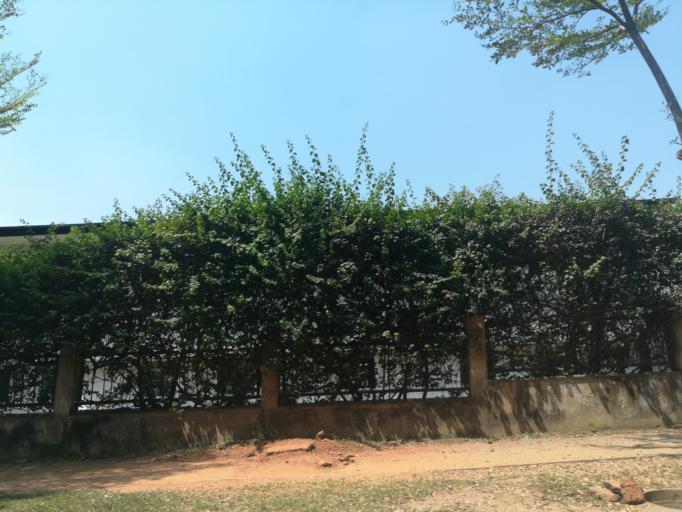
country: NG
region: Abuja Federal Capital Territory
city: Abuja
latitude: 9.0716
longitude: 7.4496
